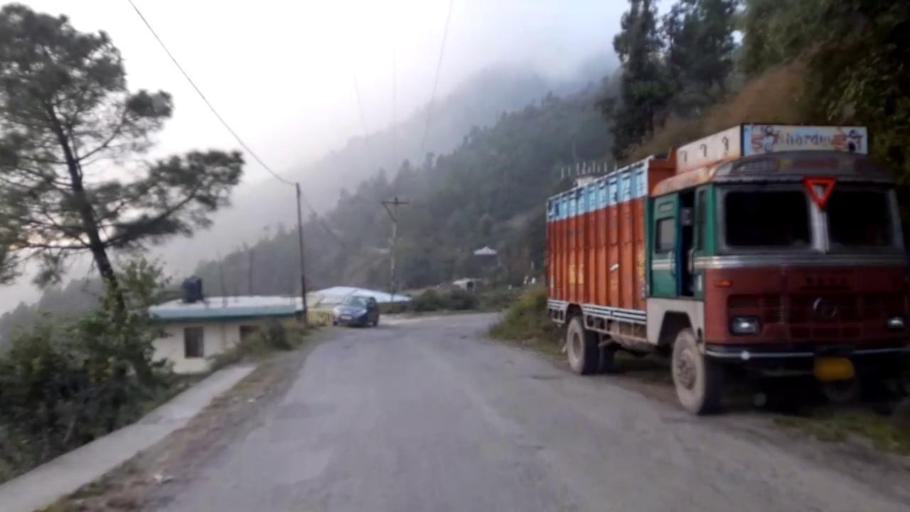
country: IN
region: Himachal Pradesh
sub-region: Shimla
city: Shimla
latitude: 31.0475
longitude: 77.1490
